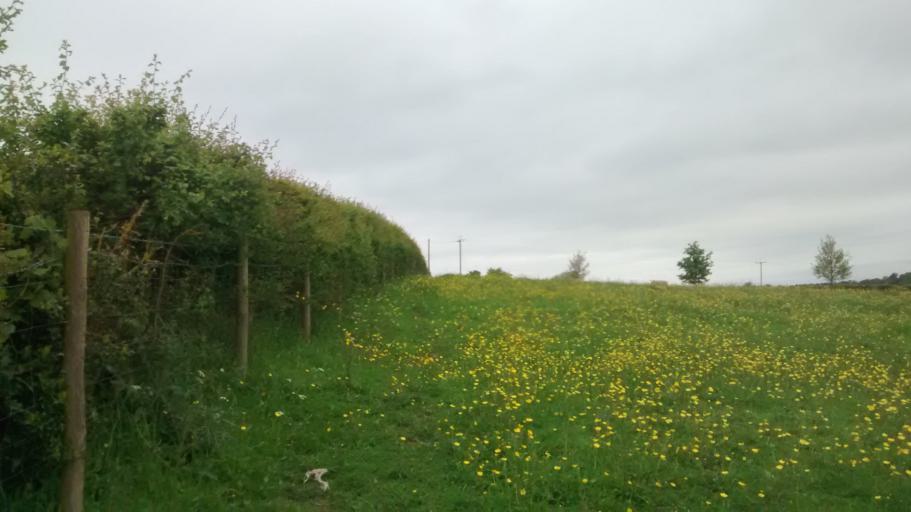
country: GB
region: England
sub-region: County Durham
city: Pittington
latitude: 54.7836
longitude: -1.5052
